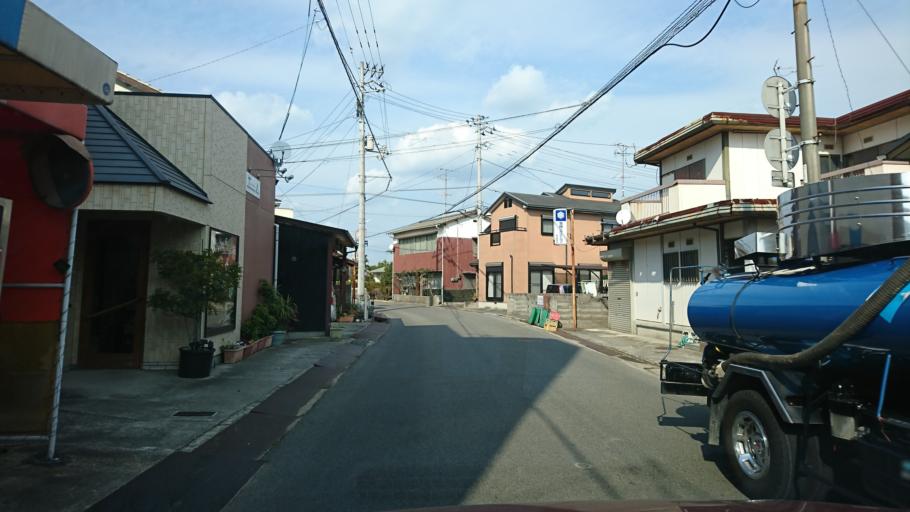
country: JP
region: Ehime
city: Saijo
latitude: 34.0228
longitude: 133.0392
